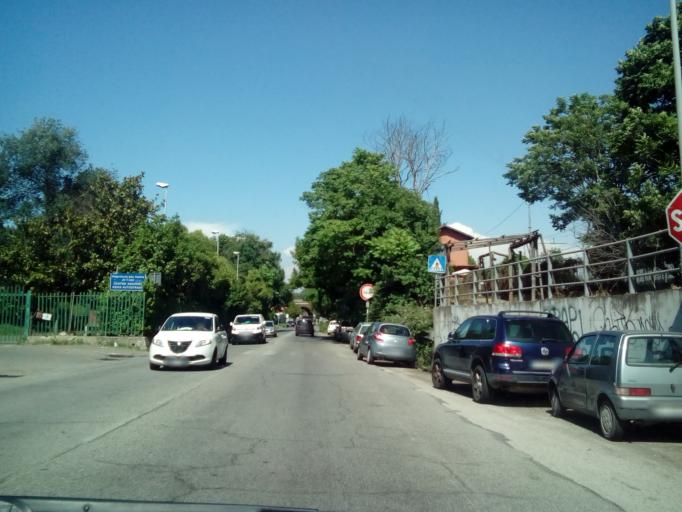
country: VA
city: Vatican City
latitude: 41.8404
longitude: 12.4638
